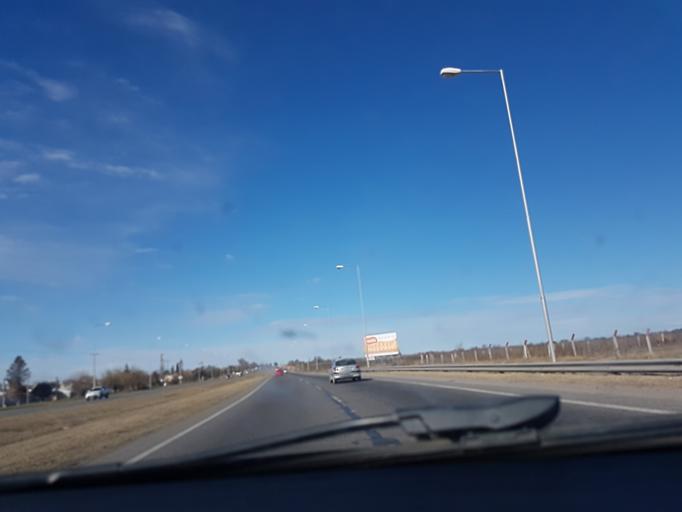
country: AR
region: Cordoba
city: La Calera
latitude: -31.4028
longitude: -64.2696
